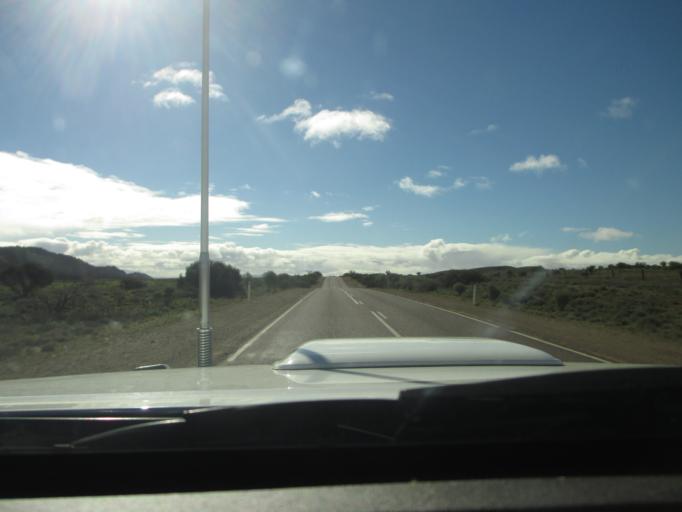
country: AU
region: South Australia
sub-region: Flinders Ranges
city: Quorn
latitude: -31.9364
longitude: 138.4100
